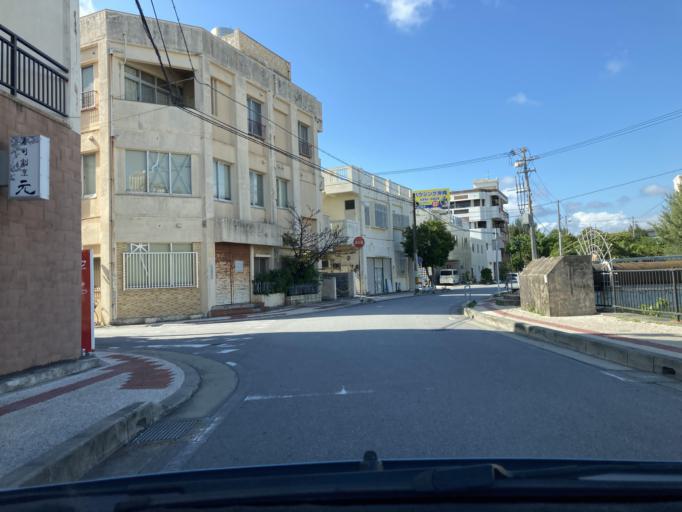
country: JP
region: Okinawa
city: Naha-shi
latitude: 26.2227
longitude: 127.6788
